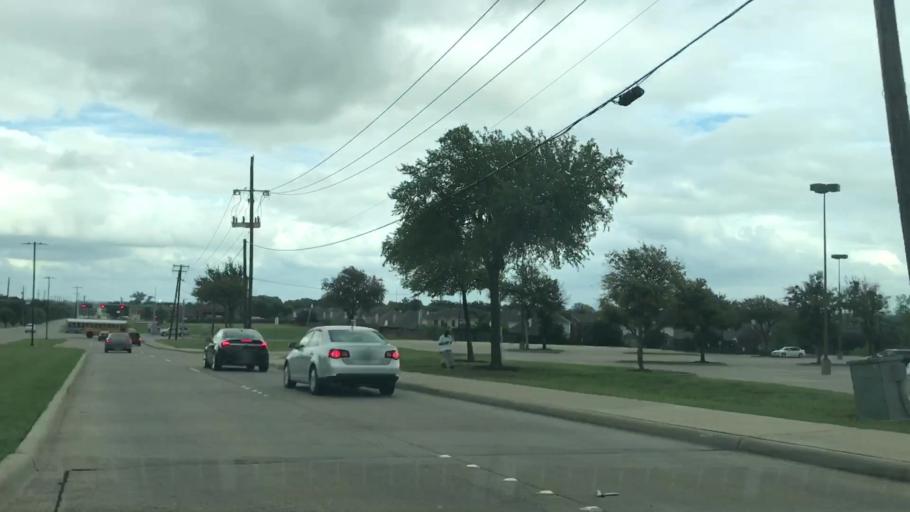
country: US
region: Texas
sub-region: Dallas County
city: Garland
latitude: 32.8942
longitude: -96.6155
